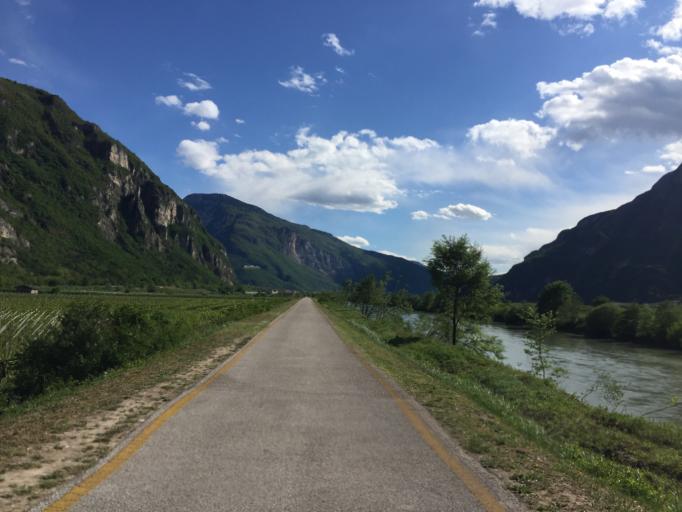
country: IT
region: Trentino-Alto Adige
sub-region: Provincia di Trento
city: Aldeno
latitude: 45.9764
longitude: 11.1097
